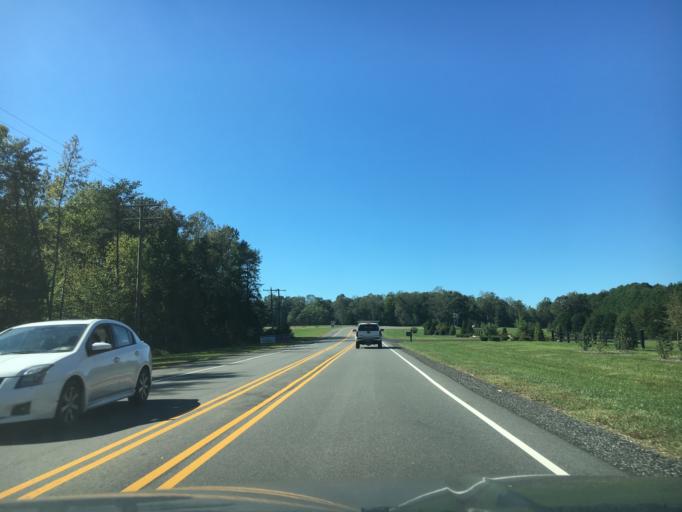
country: US
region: Virginia
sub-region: Goochland County
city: Goochland
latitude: 37.6982
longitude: -77.8291
